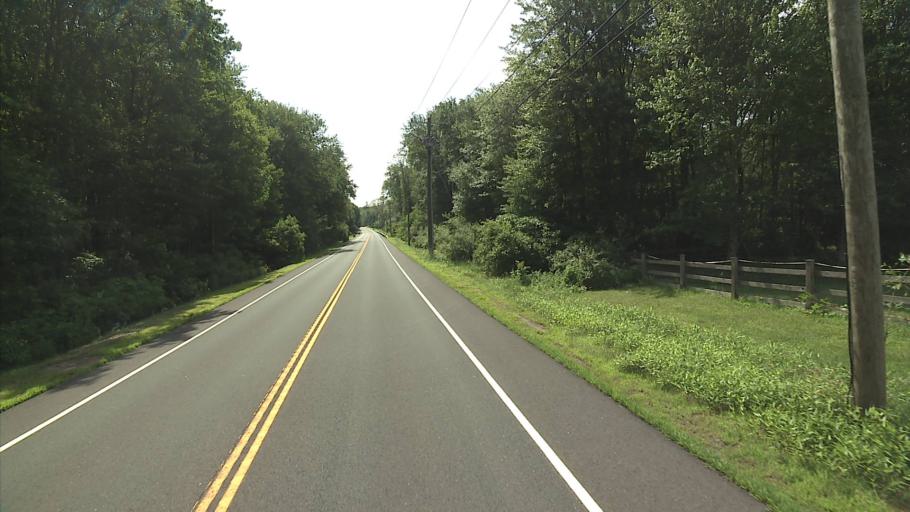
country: US
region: Connecticut
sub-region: Tolland County
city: Tolland
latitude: 41.8346
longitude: -72.4039
